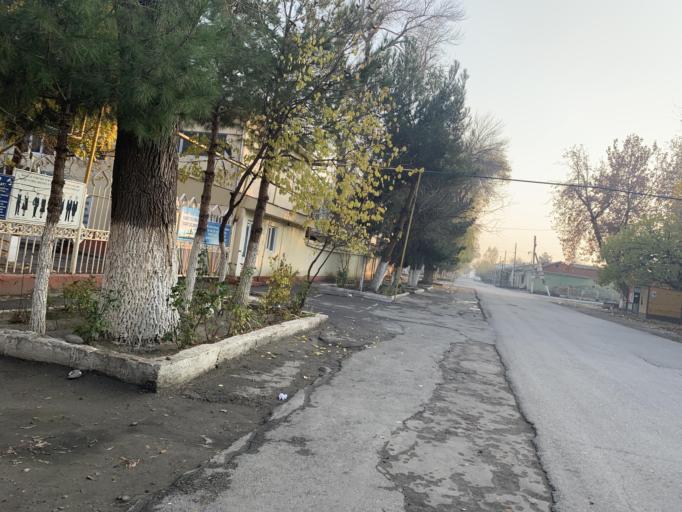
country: UZ
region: Fergana
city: Qo`qon
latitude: 40.5232
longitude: 70.9383
